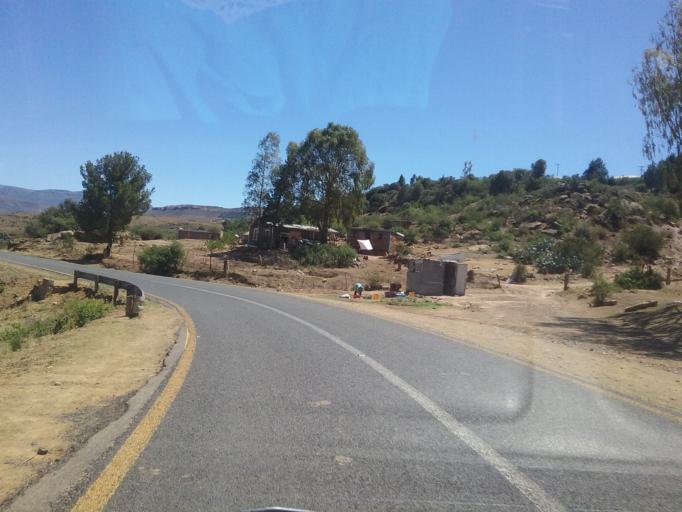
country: LS
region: Quthing
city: Quthing
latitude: -30.2930
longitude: 27.7651
